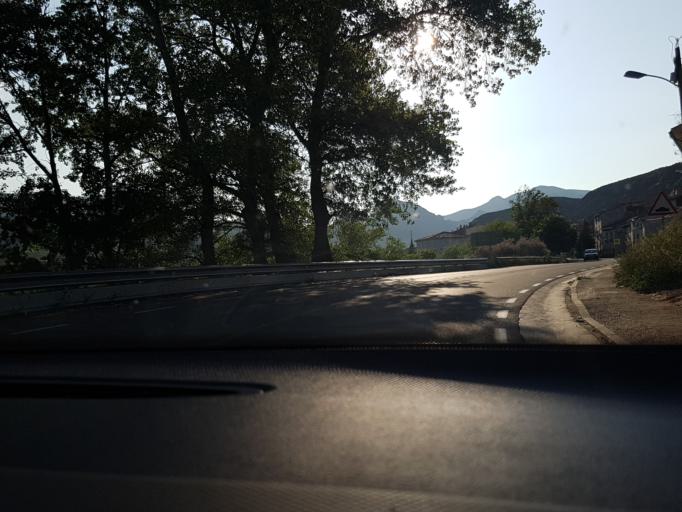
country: ES
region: La Rioja
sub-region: Provincia de La Rioja
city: Santa Eulalia Bajera
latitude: 42.2091
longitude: -2.1890
